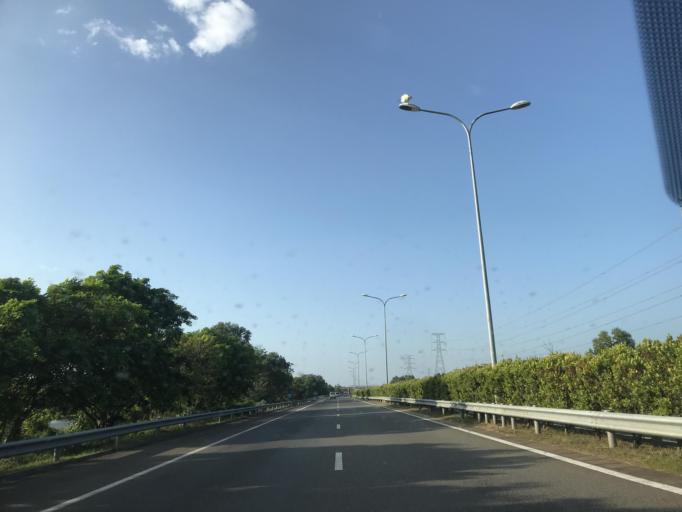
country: LK
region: Western
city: Kandana
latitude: 7.0447
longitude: 79.8833
